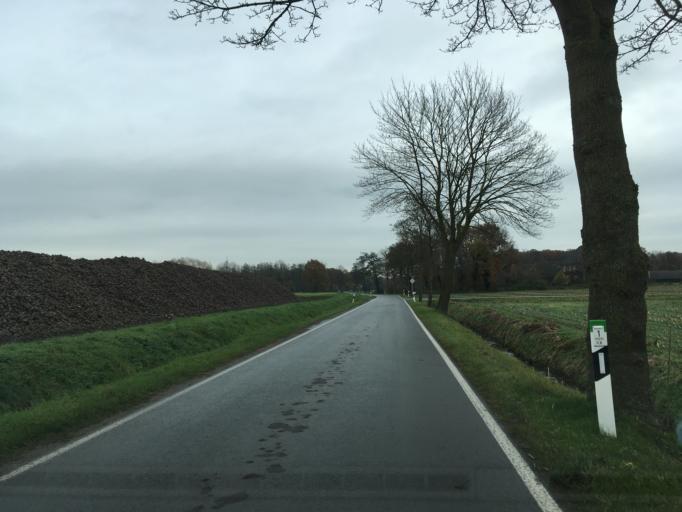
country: DE
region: North Rhine-Westphalia
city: Stadtlohn
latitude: 52.0101
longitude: 6.9520
